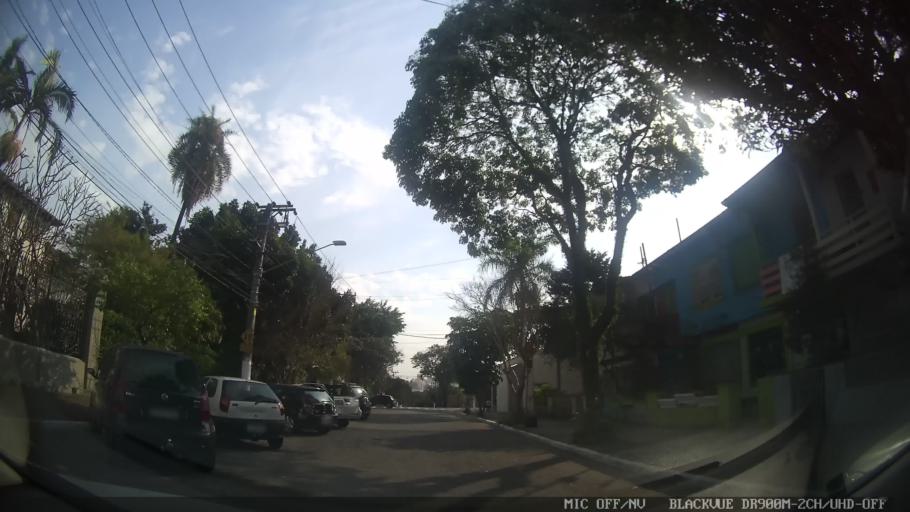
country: BR
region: Sao Paulo
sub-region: Sao Paulo
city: Sao Paulo
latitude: -23.5908
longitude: -46.6110
